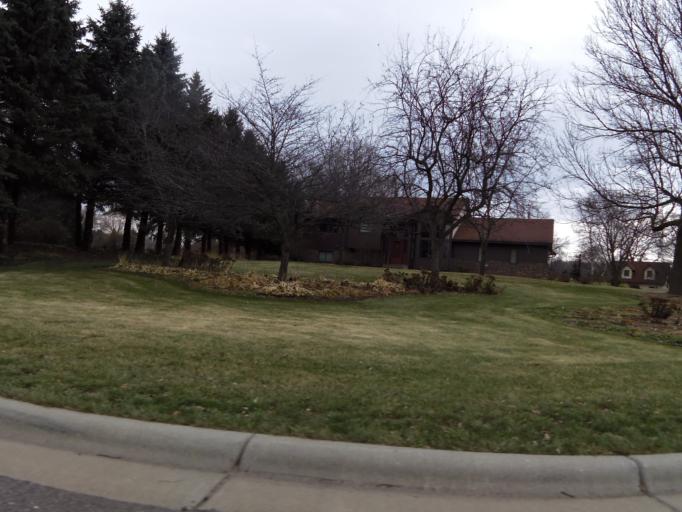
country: US
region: Minnesota
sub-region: Washington County
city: Lake Elmo
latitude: 44.9835
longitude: -92.8748
